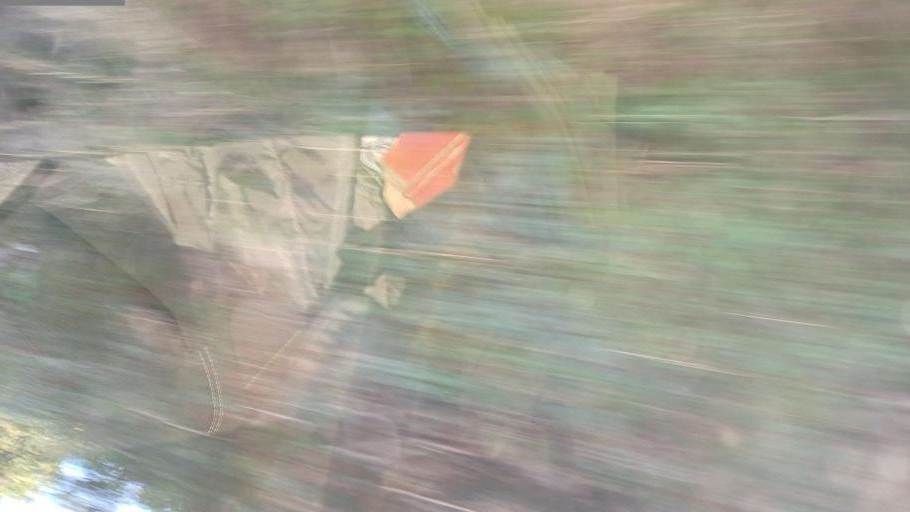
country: CY
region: Pafos
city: Pegeia
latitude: 34.9079
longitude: 32.3340
